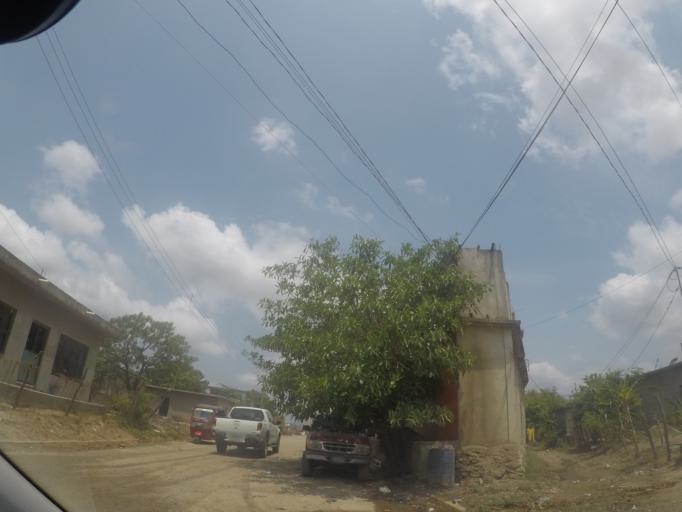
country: MX
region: Oaxaca
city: El Espinal
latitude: 16.5513
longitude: -94.9439
